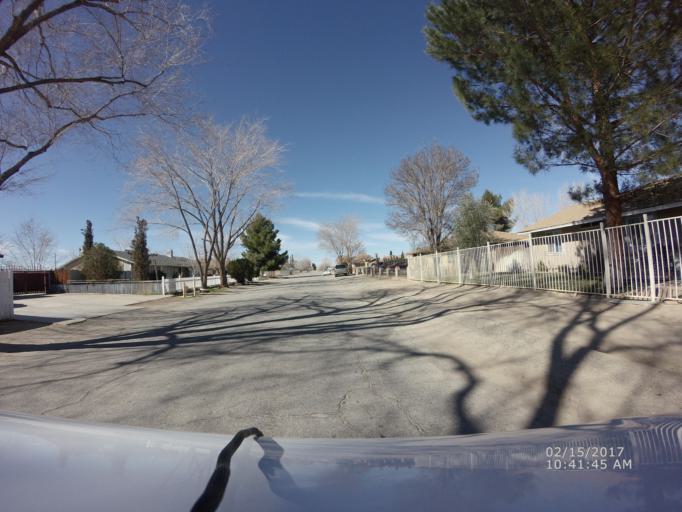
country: US
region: California
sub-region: Los Angeles County
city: Lake Los Angeles
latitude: 34.5813
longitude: -117.8562
